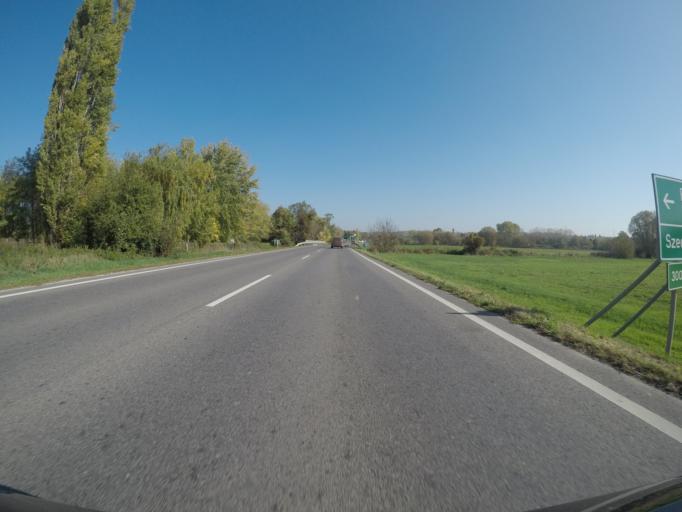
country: HU
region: Baranya
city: Pecsvarad
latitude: 46.1519
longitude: 18.4199
